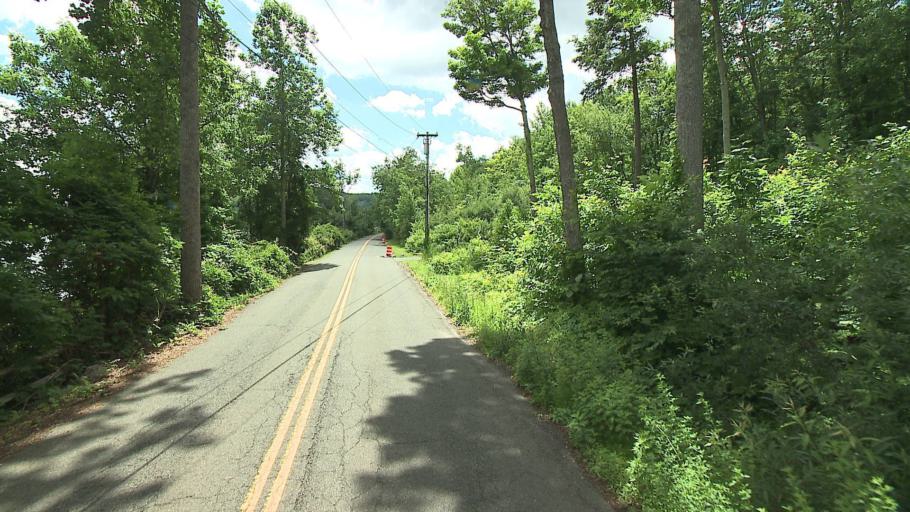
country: US
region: Connecticut
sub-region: Litchfield County
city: New Preston
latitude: 41.7006
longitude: -73.3799
